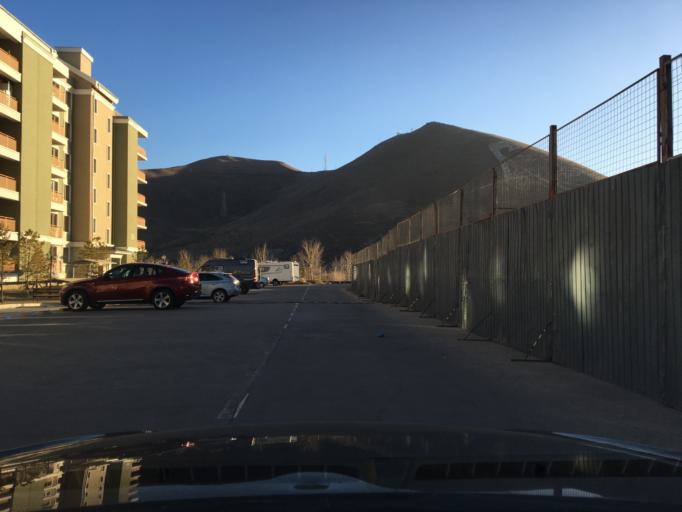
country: MN
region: Ulaanbaatar
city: Ulaanbaatar
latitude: 47.8898
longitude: 106.9286
